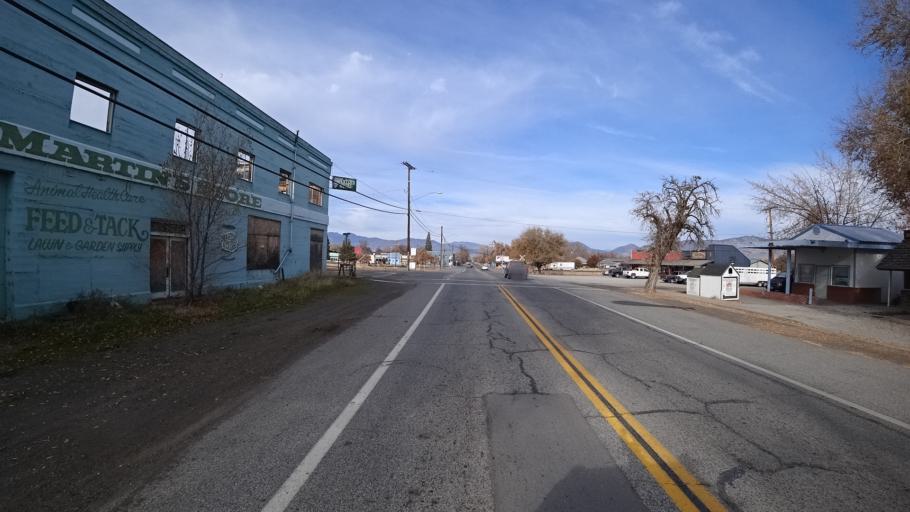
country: US
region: California
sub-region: Siskiyou County
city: Montague
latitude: 41.7274
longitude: -122.5256
